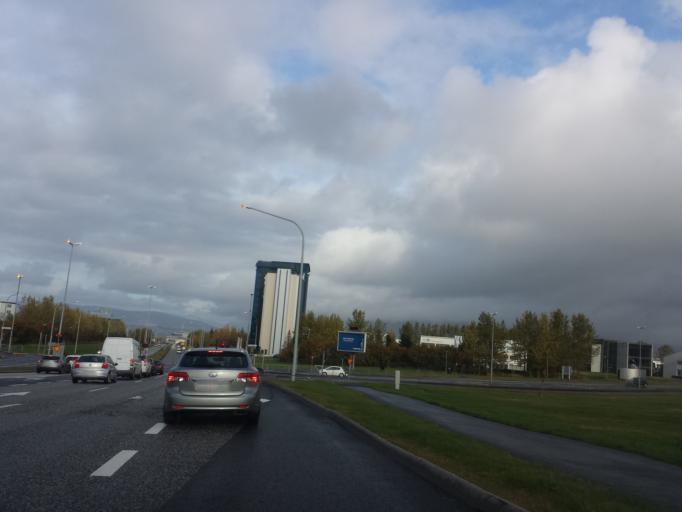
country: IS
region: Capital Region
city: Reykjavik
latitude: 64.1392
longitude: -21.8931
